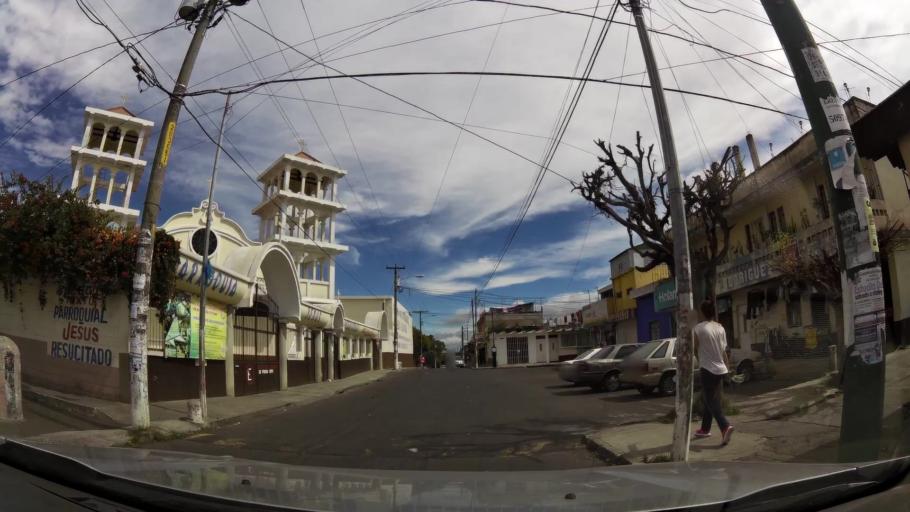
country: GT
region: Guatemala
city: Mixco
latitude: 14.6673
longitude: -90.5703
